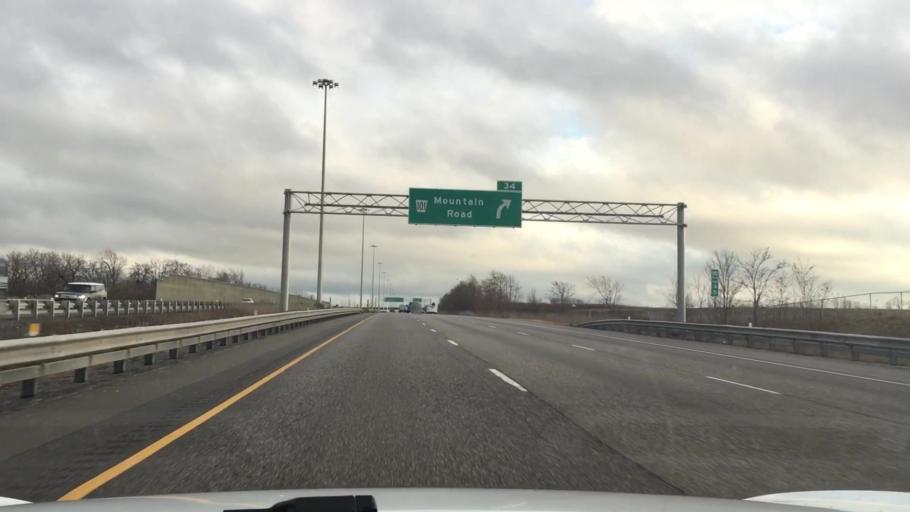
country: CA
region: Ontario
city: Thorold
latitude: 43.1424
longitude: -79.1391
